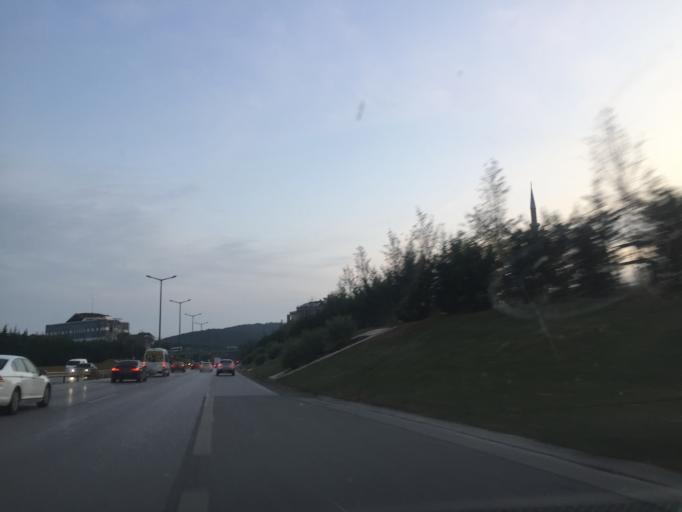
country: TR
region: Istanbul
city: Samandira
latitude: 40.9634
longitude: 29.2201
